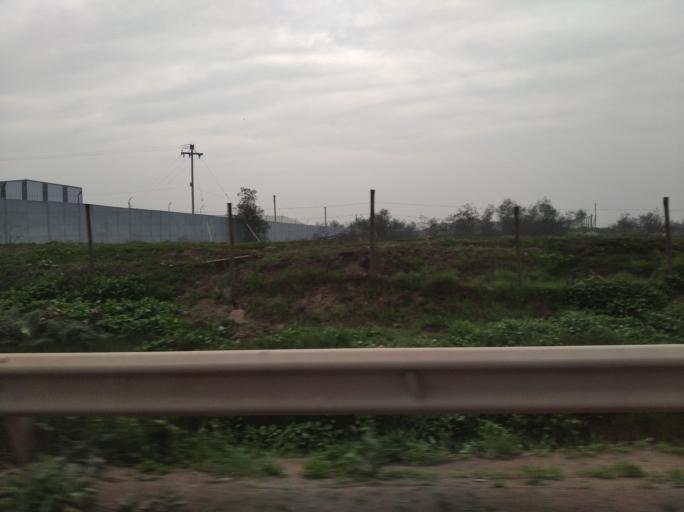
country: CL
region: Santiago Metropolitan
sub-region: Provincia de Chacabuco
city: Lampa
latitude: -33.3629
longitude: -70.7997
